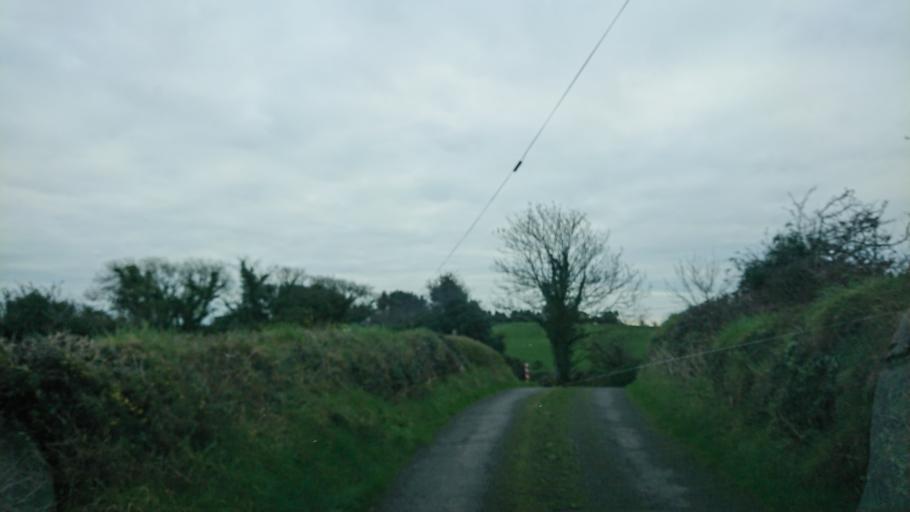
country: IE
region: Leinster
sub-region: Kilkenny
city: Mooncoin
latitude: 52.2102
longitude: -7.2672
